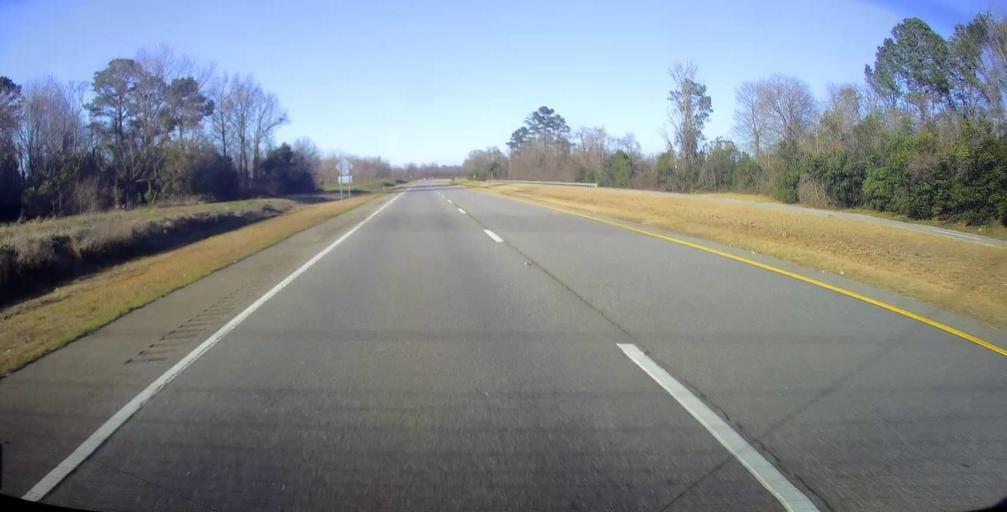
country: US
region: Georgia
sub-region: Sumter County
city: Americus
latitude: 31.9518
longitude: -84.2558
